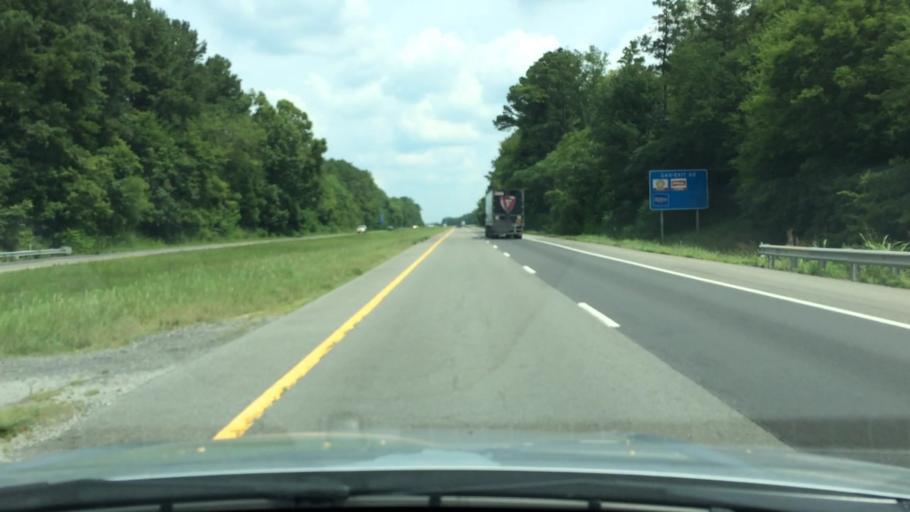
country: US
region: Tennessee
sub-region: Marshall County
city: Cornersville
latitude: 35.2907
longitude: -86.8842
